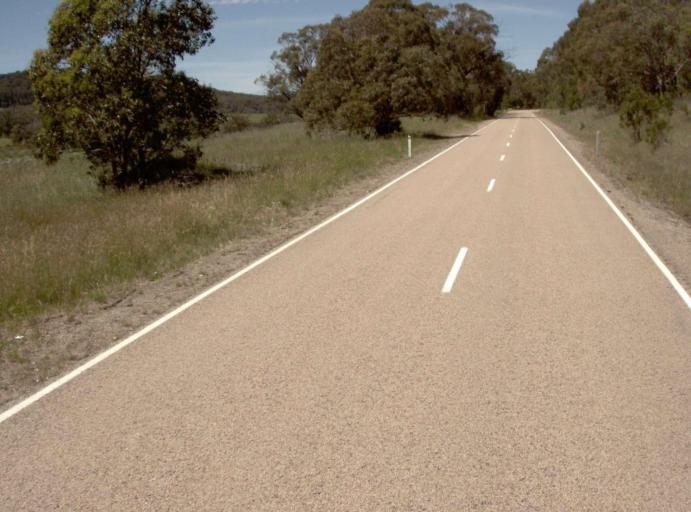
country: AU
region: Victoria
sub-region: East Gippsland
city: Lakes Entrance
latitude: -37.2075
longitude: 148.2693
